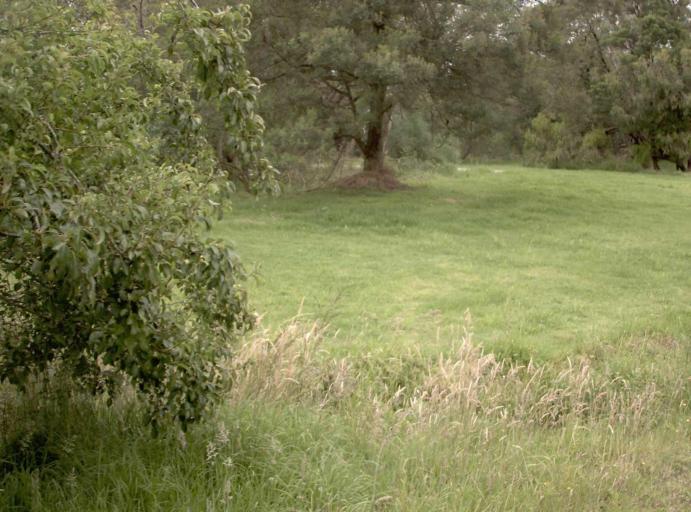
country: AU
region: Victoria
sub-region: Cardinia
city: Bunyip
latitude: -38.0817
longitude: 145.7451
